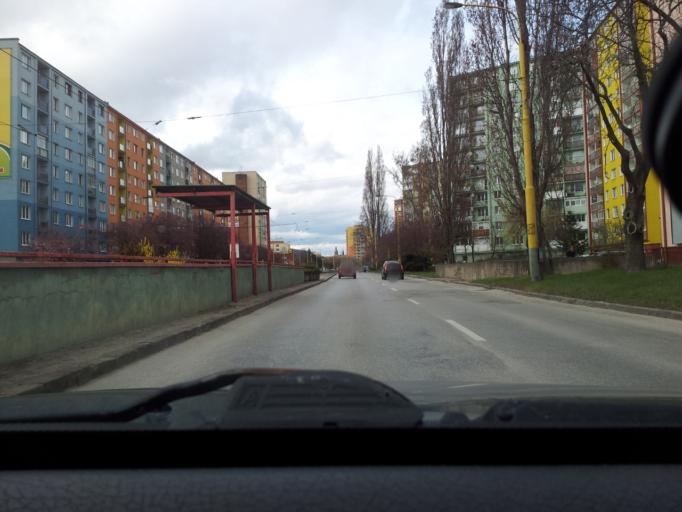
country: SK
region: Kosicky
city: Kosice
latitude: 48.7078
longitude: 21.2614
